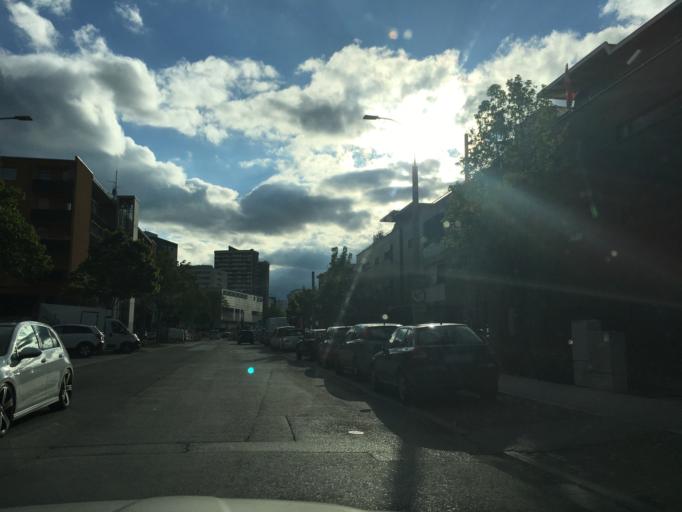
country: AT
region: Tyrol
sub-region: Politischer Bezirk Innsbruck Land
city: Ampass
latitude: 47.2742
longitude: 11.4454
